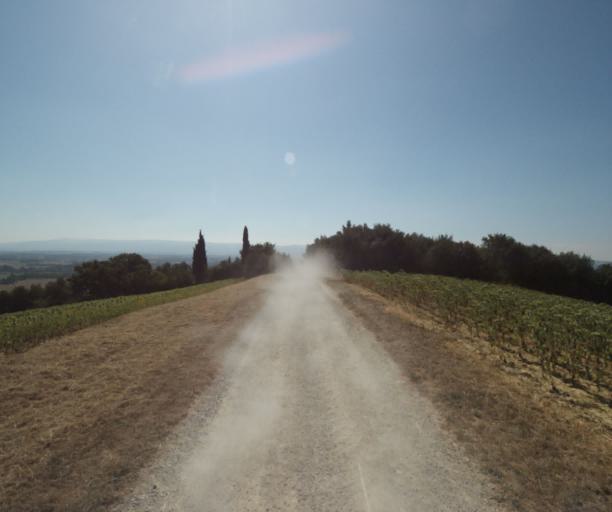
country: FR
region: Midi-Pyrenees
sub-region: Departement de la Haute-Garonne
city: Saint-Felix-Lauragais
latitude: 43.5023
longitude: 1.9355
